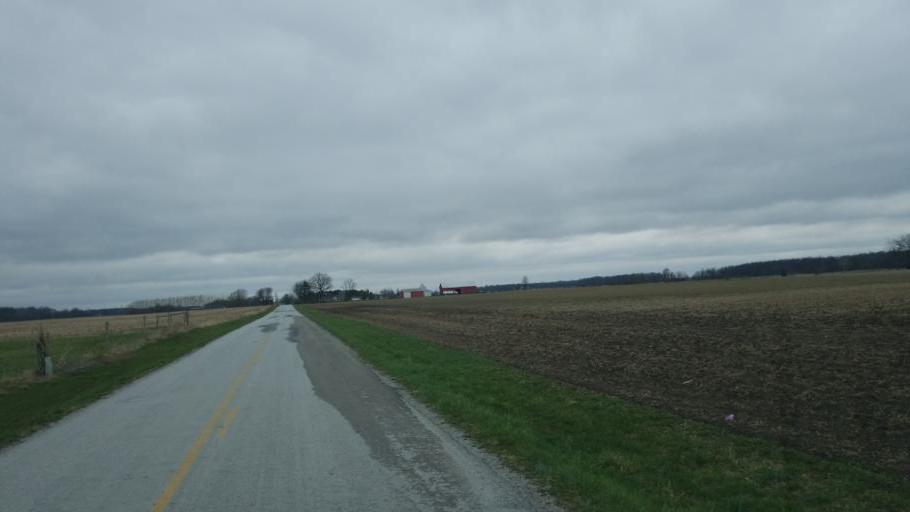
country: US
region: Ohio
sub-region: Hardin County
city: Forest
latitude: 40.7243
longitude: -83.5381
